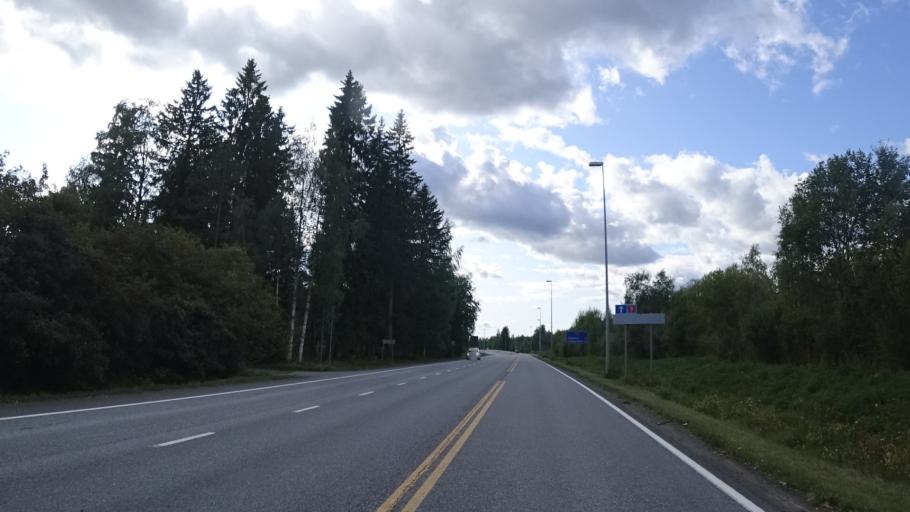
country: RU
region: Republic of Karelia
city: Vyartsilya
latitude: 62.1765
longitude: 30.5858
